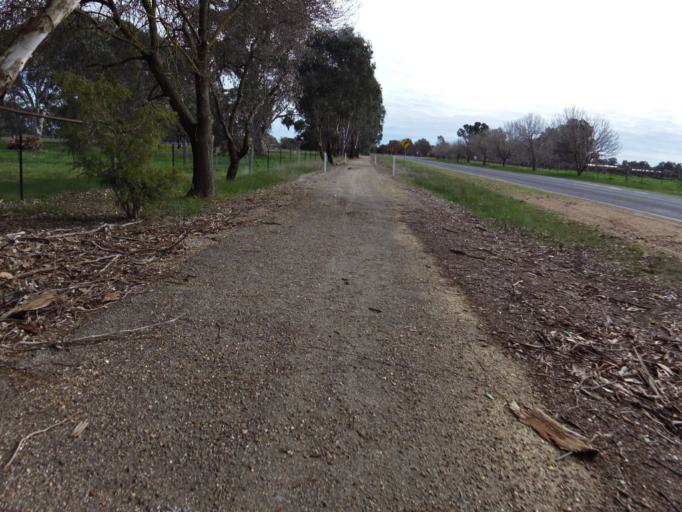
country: AU
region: Victoria
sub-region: Wangaratta
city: Wangaratta
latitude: -36.4373
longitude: 146.3590
